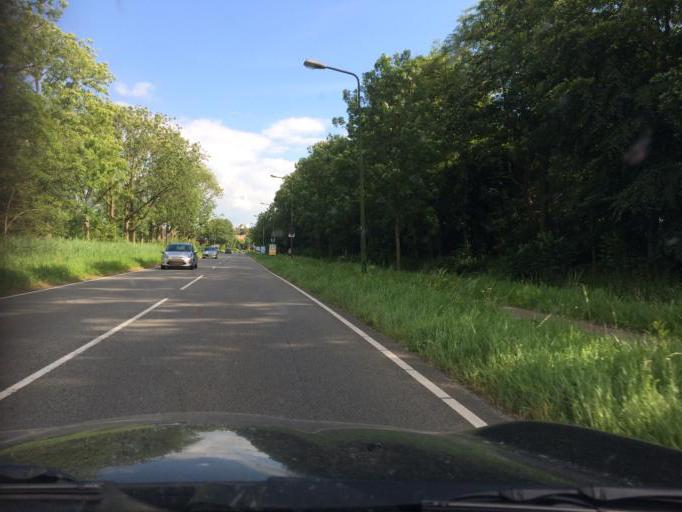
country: NL
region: Utrecht
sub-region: Gemeente Woerden
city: Woerden
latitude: 52.0937
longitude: 4.8919
